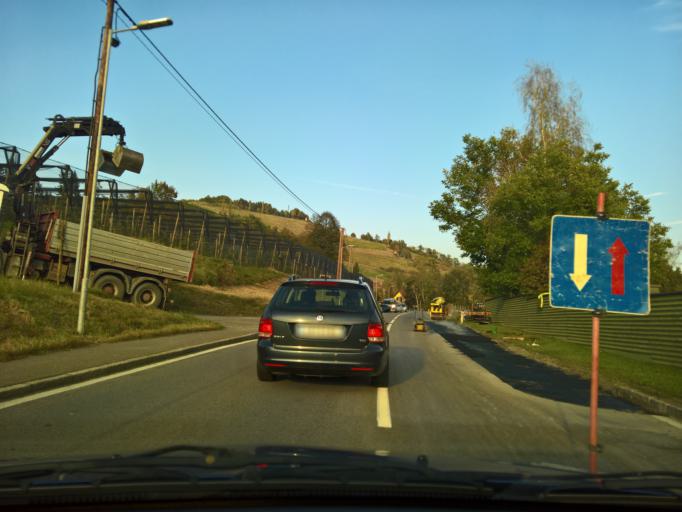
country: AT
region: Styria
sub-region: Politischer Bezirk Leibnitz
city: Seggauberg
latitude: 46.7763
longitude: 15.5084
